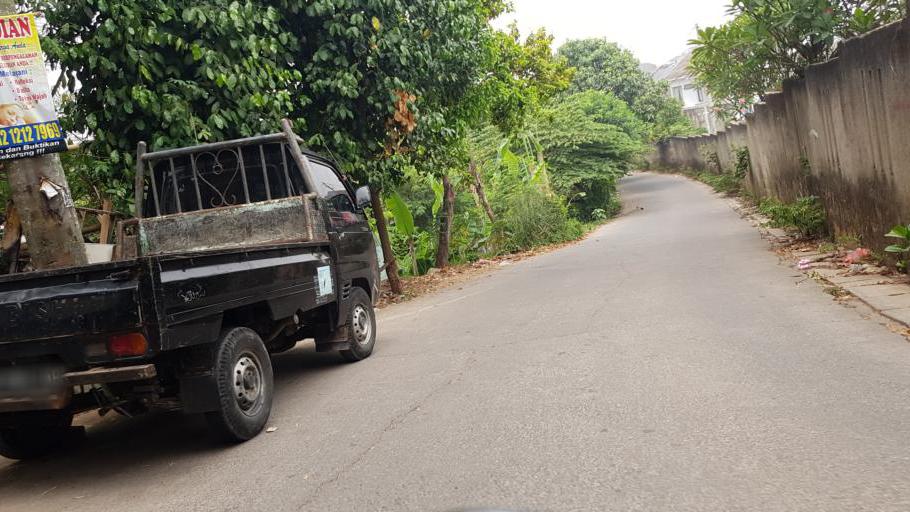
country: ID
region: West Java
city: Pamulang
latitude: -6.3316
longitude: 106.8010
